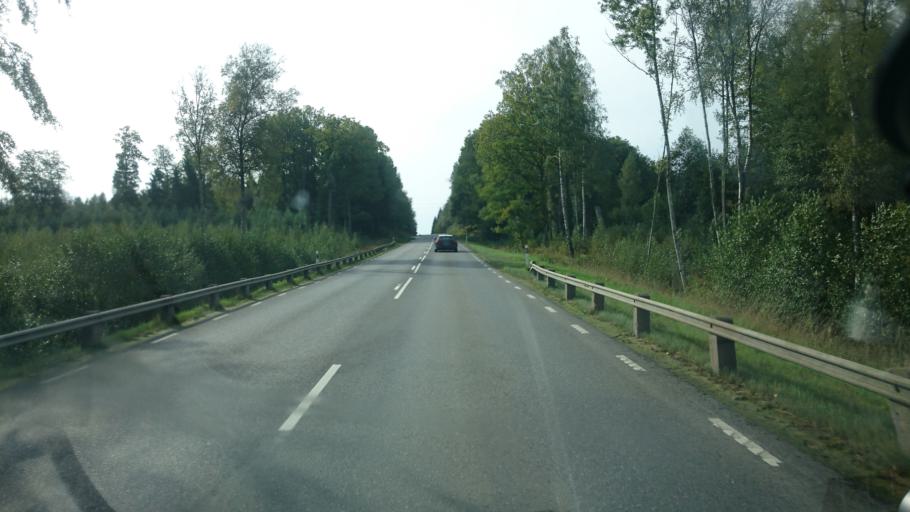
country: SE
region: Vaestra Goetaland
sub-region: Alingsas Kommun
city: Sollebrunn
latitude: 58.0317
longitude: 12.4637
